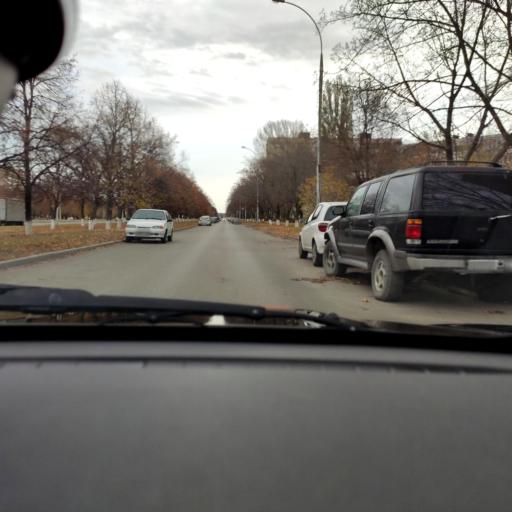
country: RU
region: Samara
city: Tol'yatti
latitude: 53.5209
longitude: 49.2619
